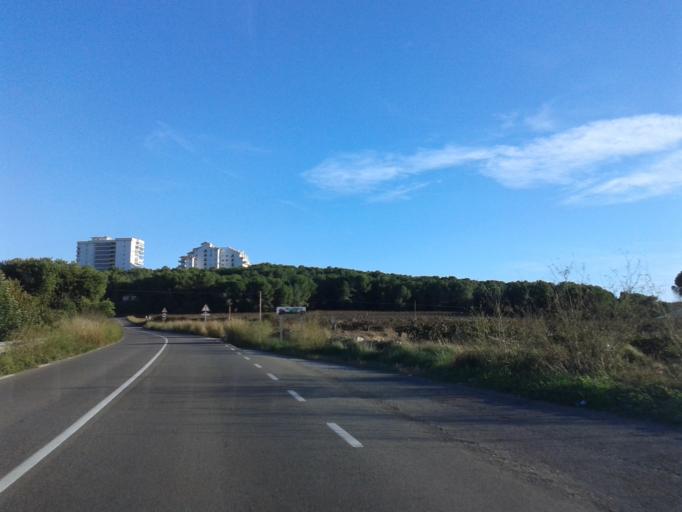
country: ES
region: Catalonia
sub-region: Provincia de Barcelona
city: Sitges
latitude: 41.2470
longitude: 1.7888
